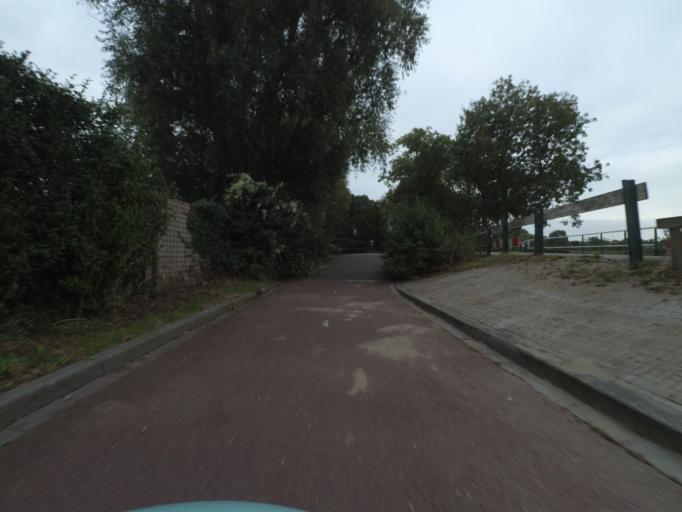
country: NL
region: Utrecht
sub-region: Gemeente Wijk bij Duurstede
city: Wijk bij Duurstede
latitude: 51.9865
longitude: 5.3426
